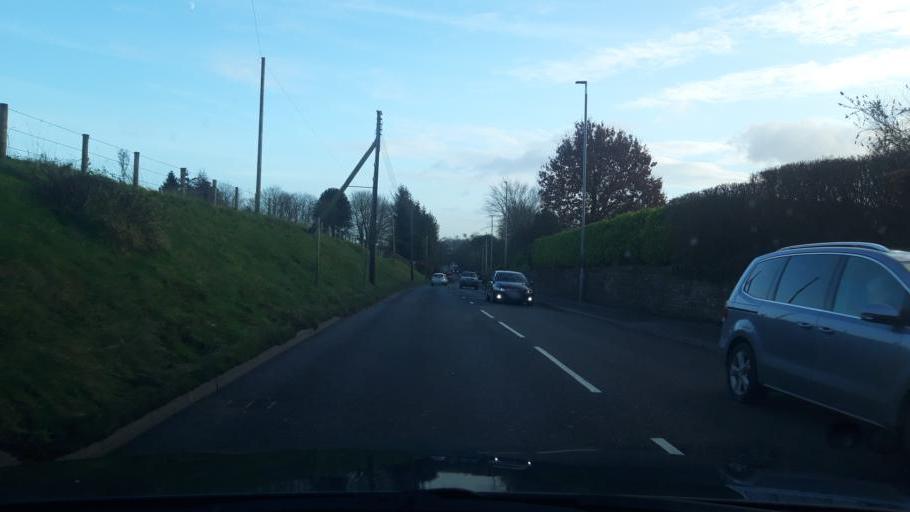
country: GB
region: Northern Ireland
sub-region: Dungannon District
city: Dungannon
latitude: 54.4935
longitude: -6.7539
